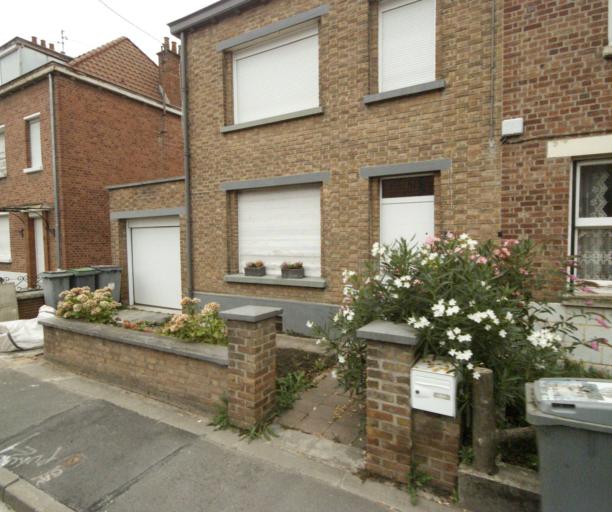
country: FR
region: Nord-Pas-de-Calais
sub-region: Departement du Nord
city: Willems
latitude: 50.6196
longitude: 3.2336
